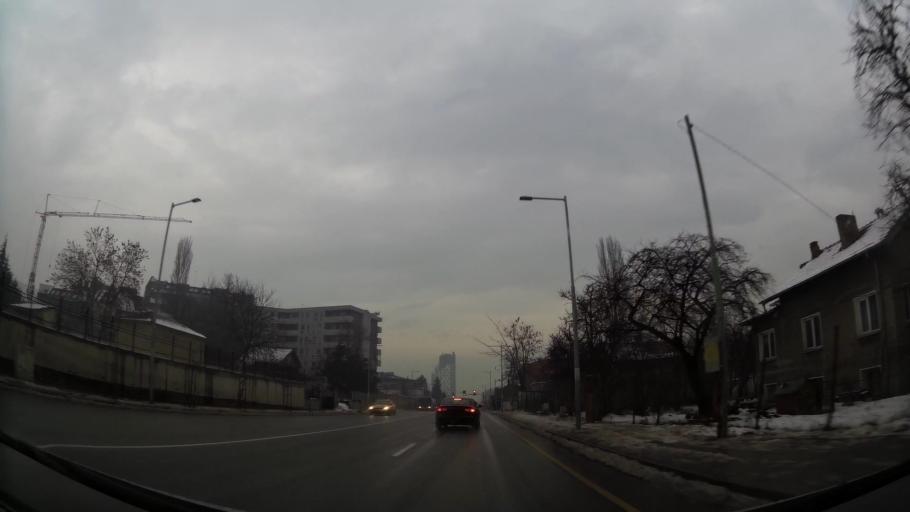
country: BG
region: Sofia-Capital
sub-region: Stolichna Obshtina
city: Sofia
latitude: 42.6758
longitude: 23.2531
